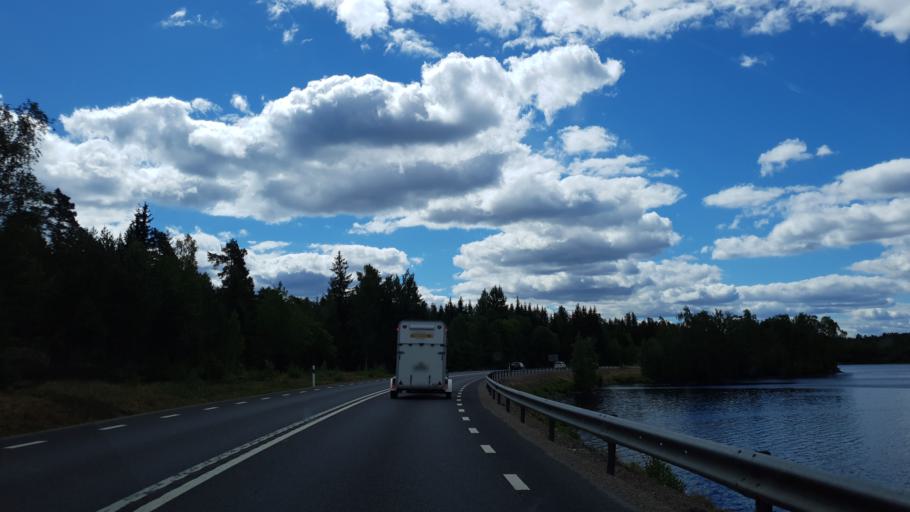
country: SE
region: Kronoberg
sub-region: Vaxjo Kommun
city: Braas
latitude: 57.2344
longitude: 15.1474
